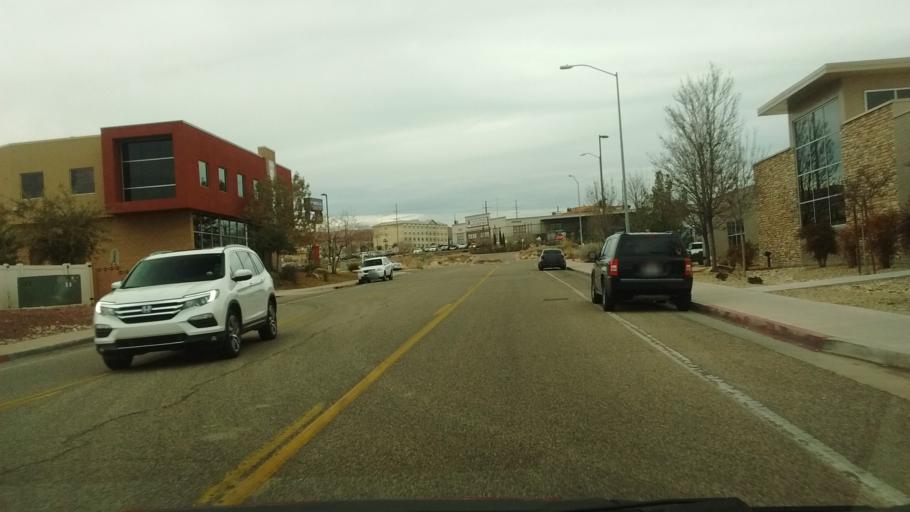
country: US
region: Utah
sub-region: Washington County
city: Washington
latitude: 37.1220
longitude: -113.5252
